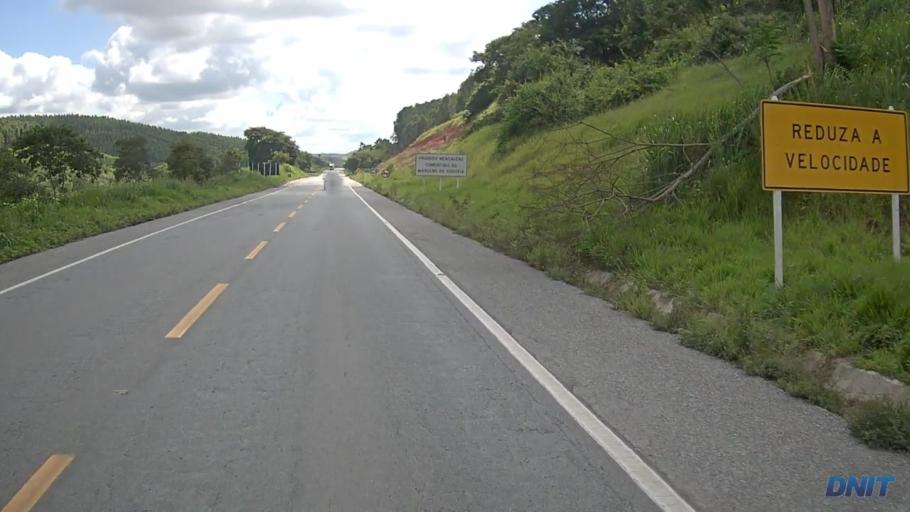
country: BR
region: Minas Gerais
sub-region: Governador Valadares
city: Governador Valadares
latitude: -19.0728
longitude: -42.1773
